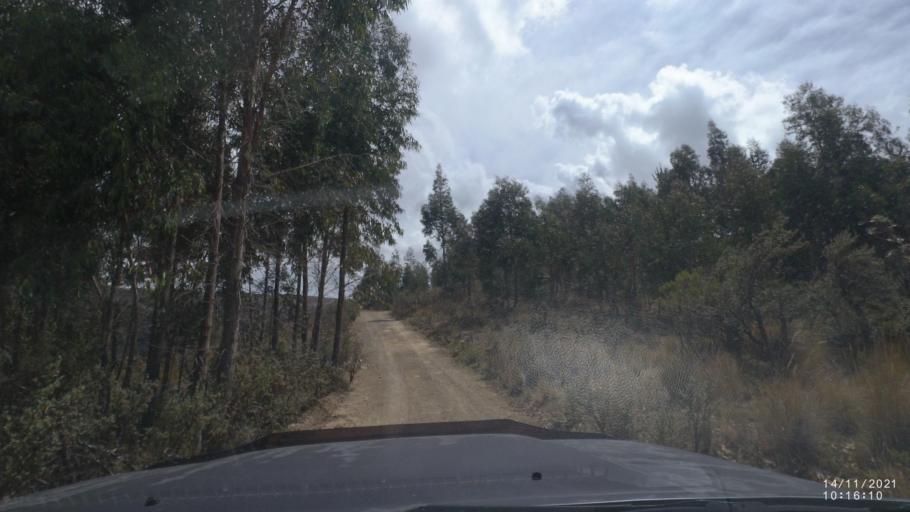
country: BO
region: Cochabamba
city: Cochabamba
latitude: -17.3421
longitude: -66.0872
